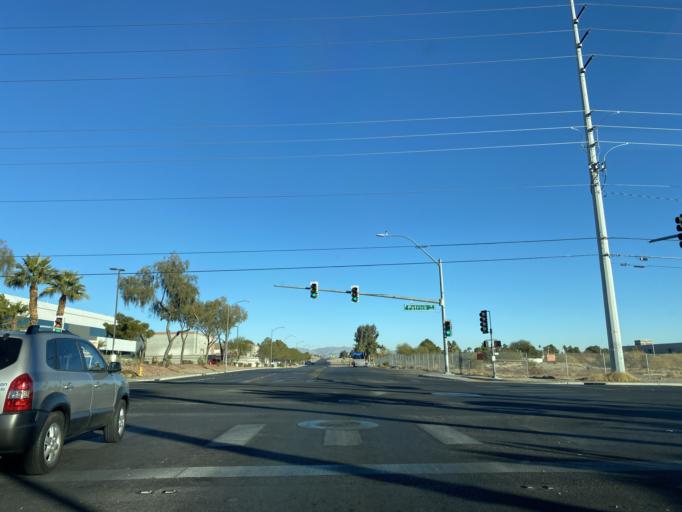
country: US
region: Nevada
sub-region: Clark County
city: Whitney
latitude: 36.0787
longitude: -115.1098
